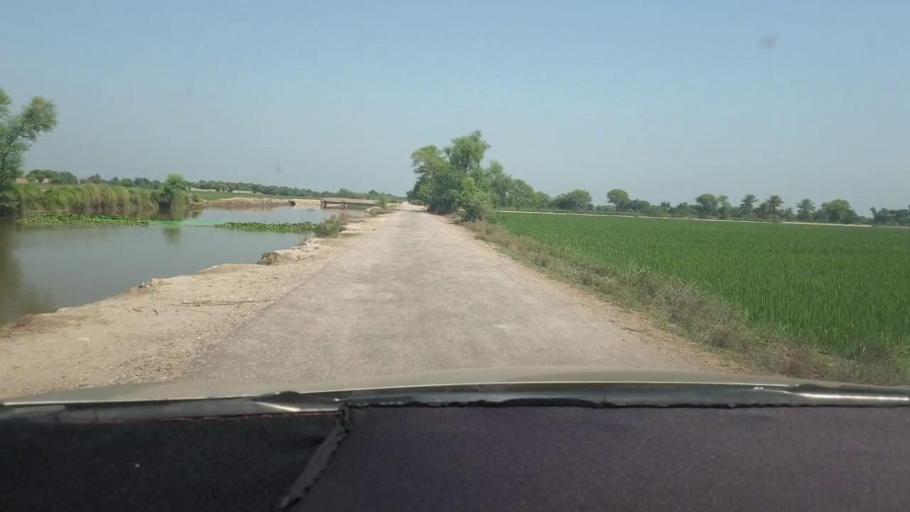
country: PK
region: Sindh
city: Miro Khan
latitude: 27.7054
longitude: 68.0757
